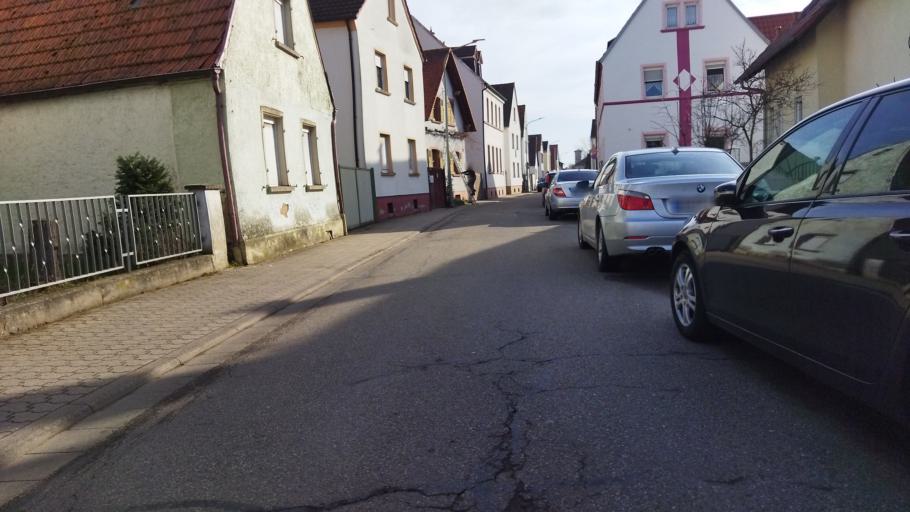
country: DE
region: Rheinland-Pfalz
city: Germersheim
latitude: 49.1920
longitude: 8.3613
